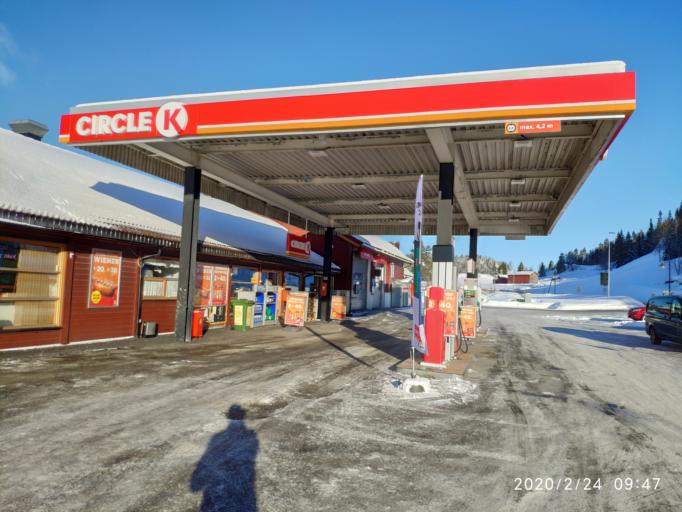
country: NO
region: Telemark
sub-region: Tokke
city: Dalen
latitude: 59.4949
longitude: 8.2031
